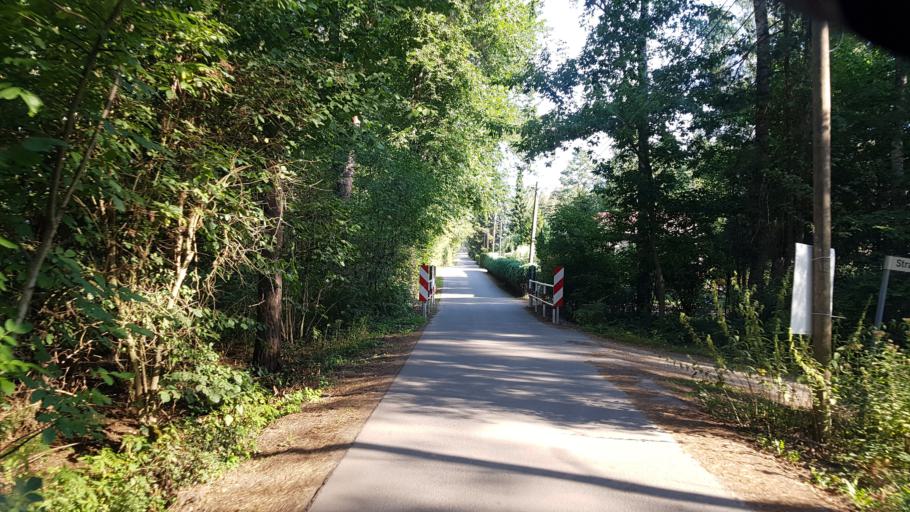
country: DE
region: Brandenburg
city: Plessa
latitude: 51.5159
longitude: 13.6511
